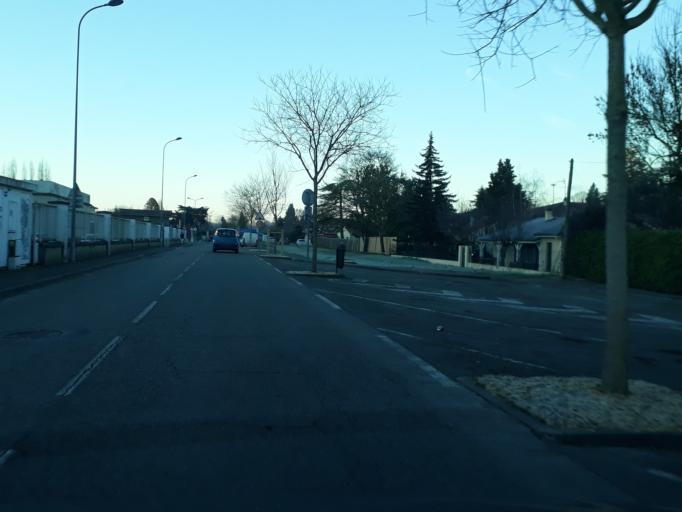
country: FR
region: Midi-Pyrenees
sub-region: Departement du Gers
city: Auch
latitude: 43.6328
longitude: 0.5890
